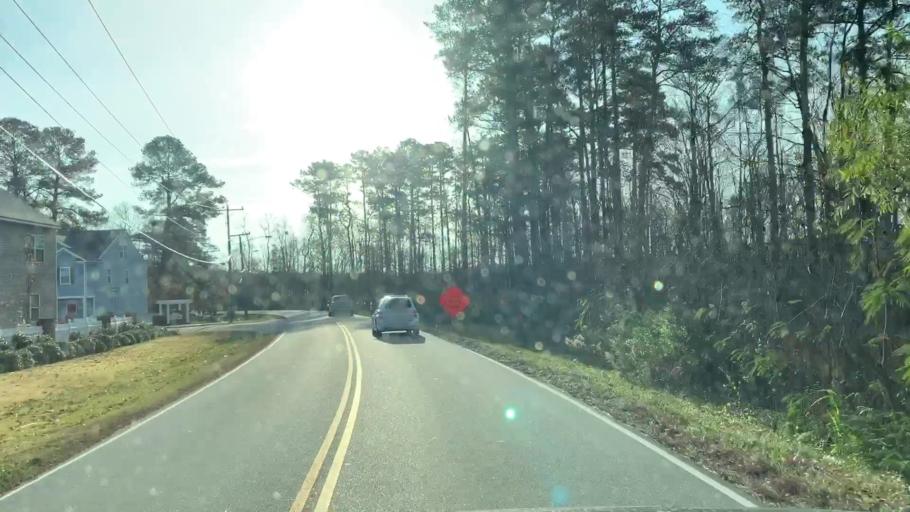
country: US
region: Virginia
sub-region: City of Chesapeake
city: Chesapeake
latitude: 36.7623
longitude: -76.1476
